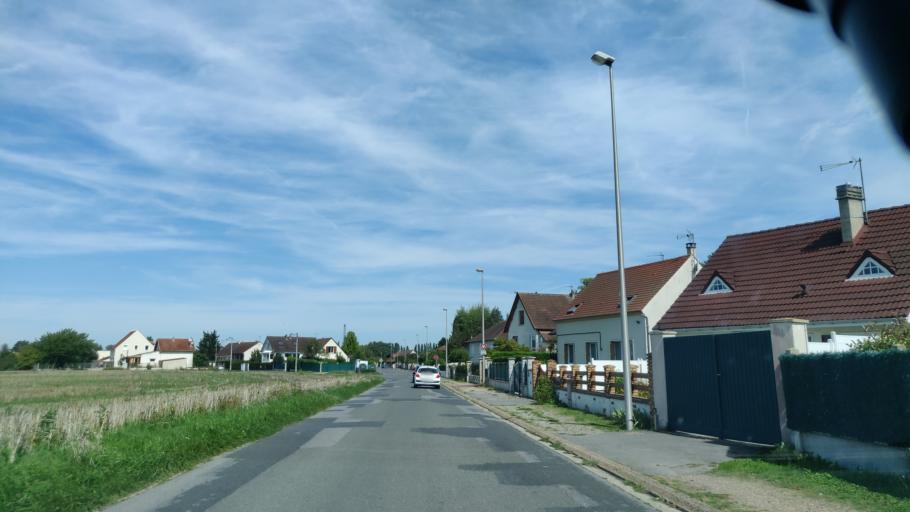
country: FR
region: Picardie
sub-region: Departement de l'Oise
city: Pont-Sainte-Maxence
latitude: 49.3080
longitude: 2.6163
